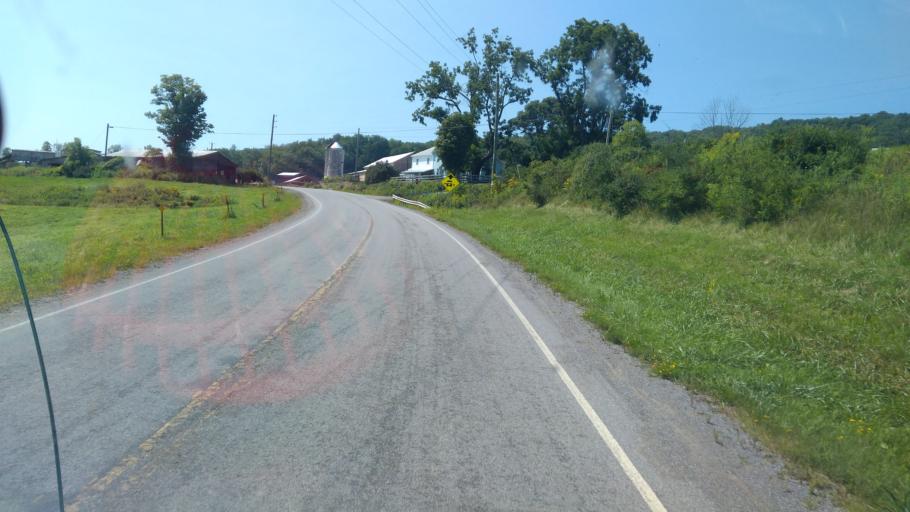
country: US
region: New York
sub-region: Allegany County
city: Belmont
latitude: 42.3209
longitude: -77.9500
